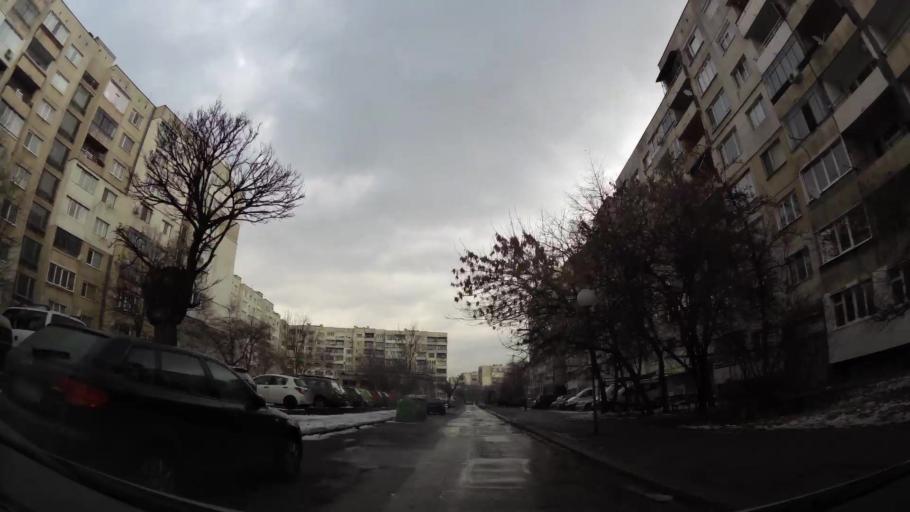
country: BG
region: Sofia-Capital
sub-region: Stolichna Obshtina
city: Sofia
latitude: 42.6974
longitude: 23.2911
